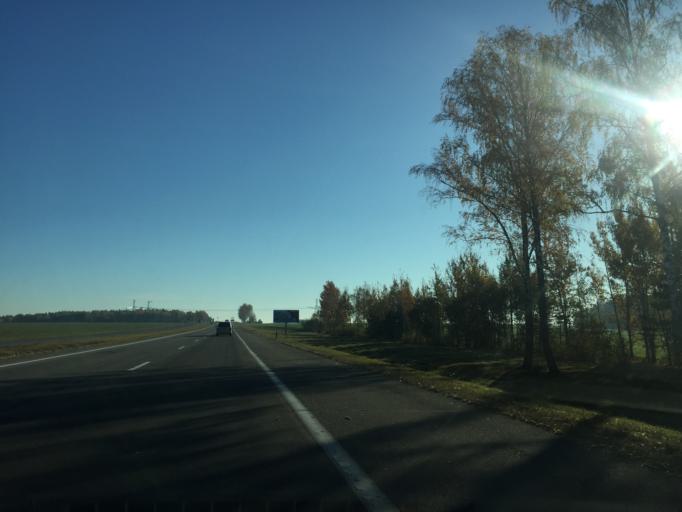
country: BY
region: Minsk
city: Smilavichy
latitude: 53.7637
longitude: 28.1005
